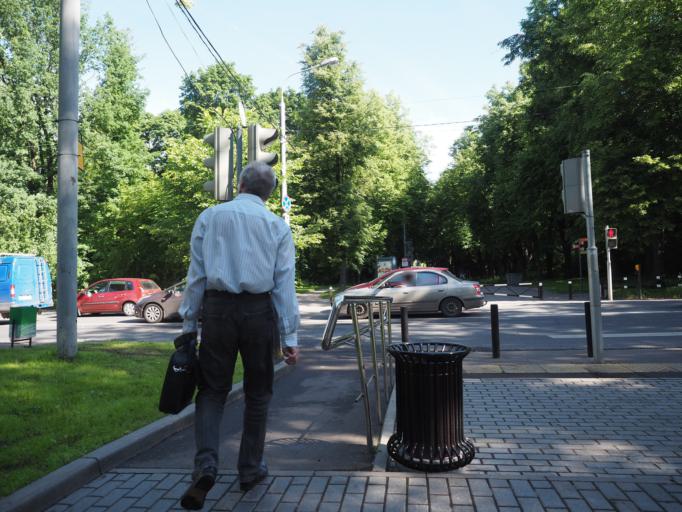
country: RU
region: Moscow
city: Ryazanskiy
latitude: 55.7763
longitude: 37.7486
